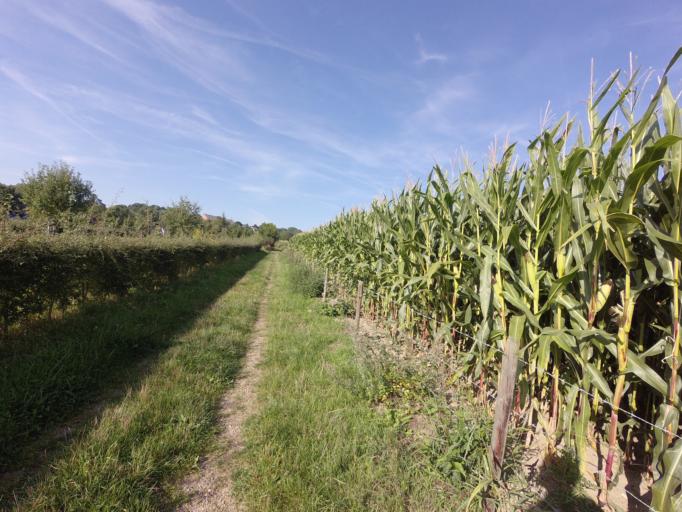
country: BE
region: Wallonia
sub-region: Province de Liege
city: Plombieres
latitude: 50.7790
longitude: 5.9118
